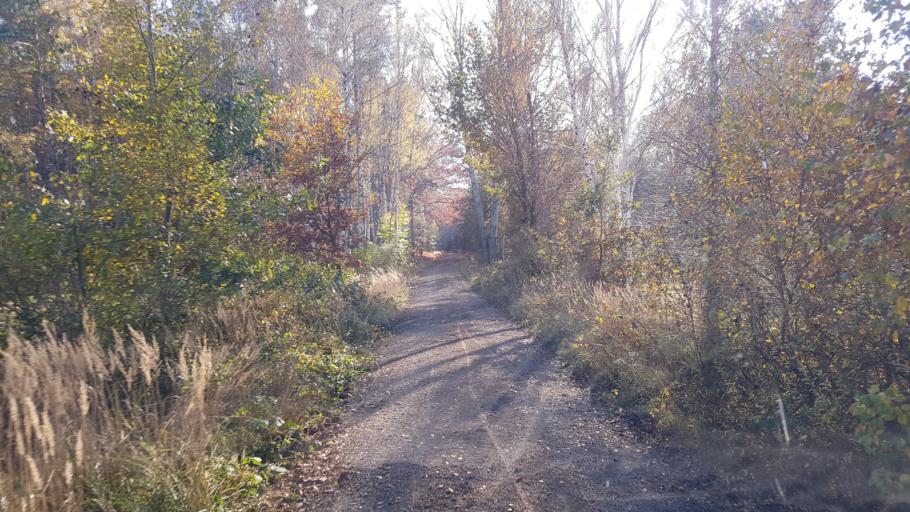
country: DE
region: Brandenburg
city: Ruckersdorf
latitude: 51.5640
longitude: 13.6211
